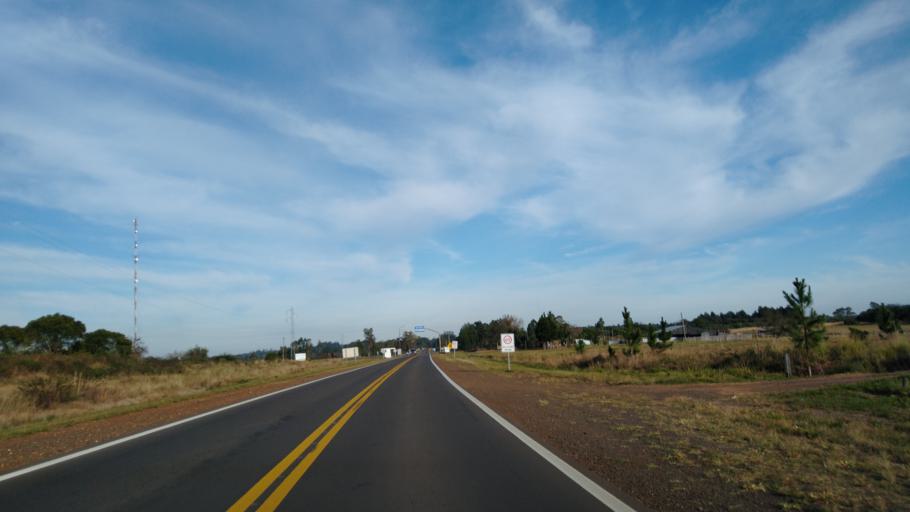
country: AR
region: Corrientes
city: Yapeyu
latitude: -29.4215
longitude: -56.8421
